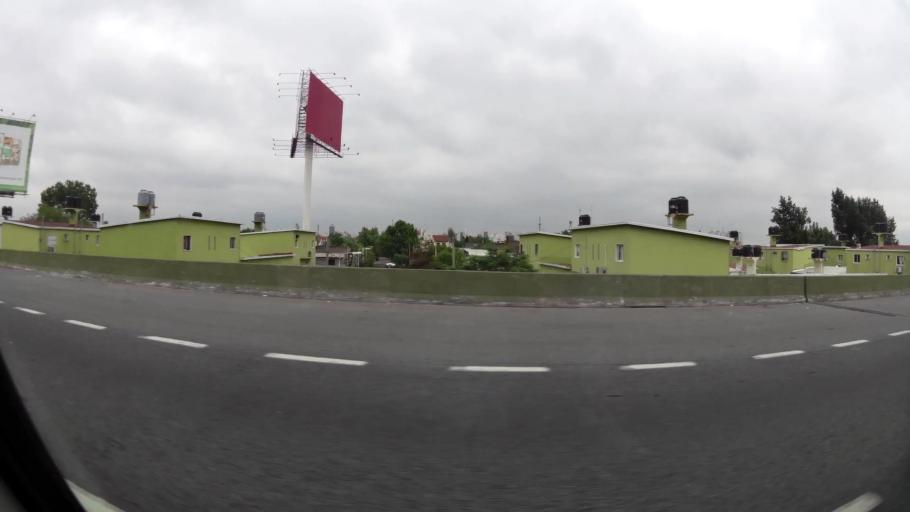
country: AR
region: Buenos Aires
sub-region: Partido de Avellaneda
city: Avellaneda
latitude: -34.6578
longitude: -58.3499
